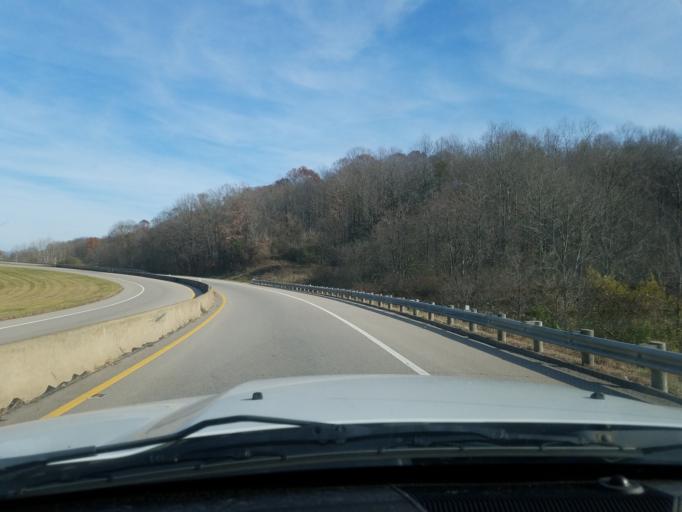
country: US
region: West Virginia
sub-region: Wood County
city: Washington
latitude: 39.2122
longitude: -81.8136
